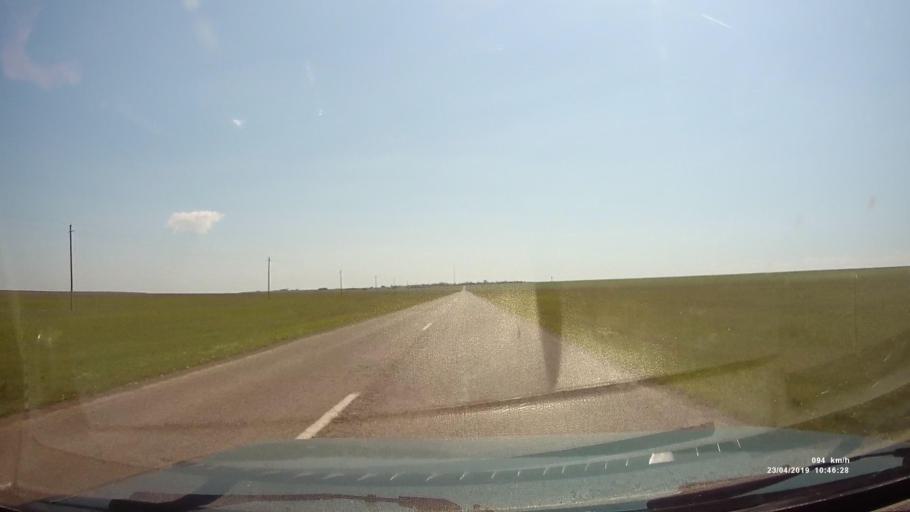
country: RU
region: Kalmykiya
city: Yashalta
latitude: 46.4427
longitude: 42.6916
